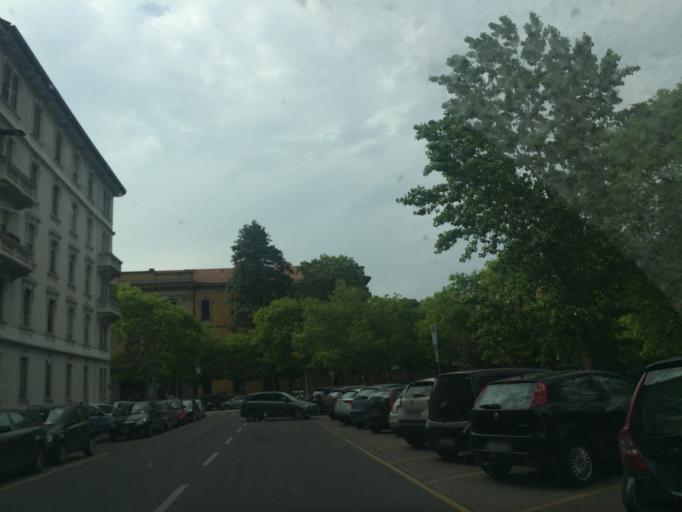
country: IT
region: Lombardy
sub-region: Citta metropolitana di Milano
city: Milano
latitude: 45.4891
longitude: 9.1597
